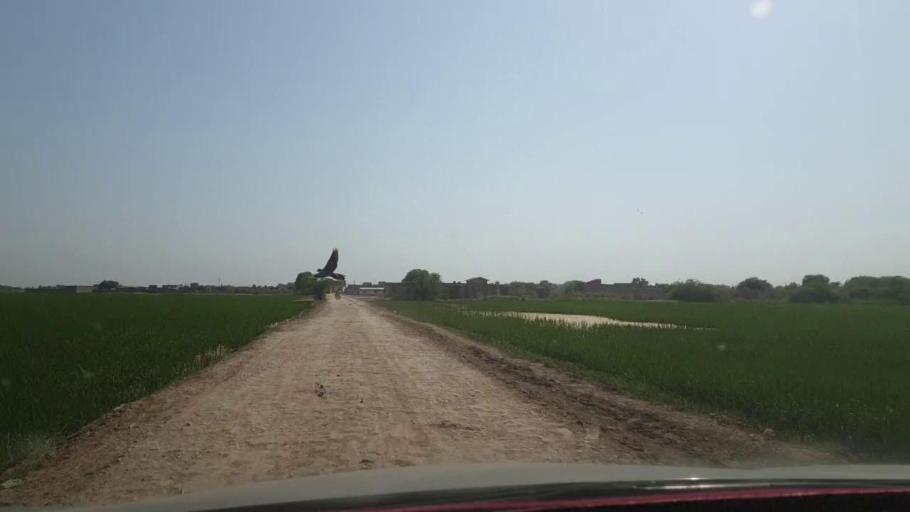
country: PK
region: Sindh
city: Nasirabad
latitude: 27.3495
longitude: 67.8427
